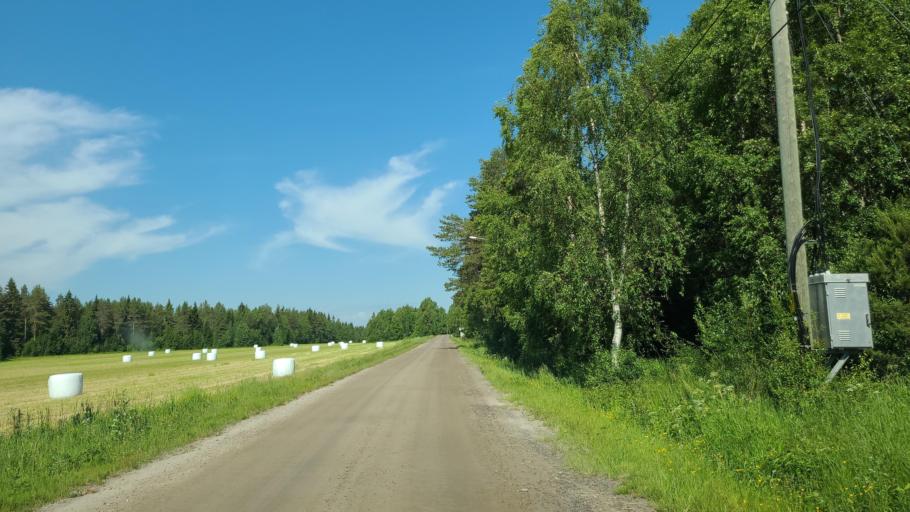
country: SE
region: Vaesterbotten
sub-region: Robertsfors Kommun
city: Robertsfors
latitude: 64.0826
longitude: 20.8467
